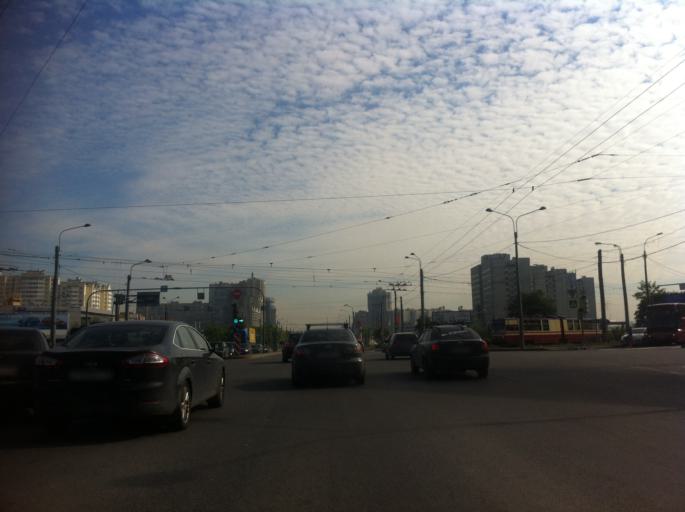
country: RU
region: St.-Petersburg
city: Uritsk
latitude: 59.8455
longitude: 30.2122
